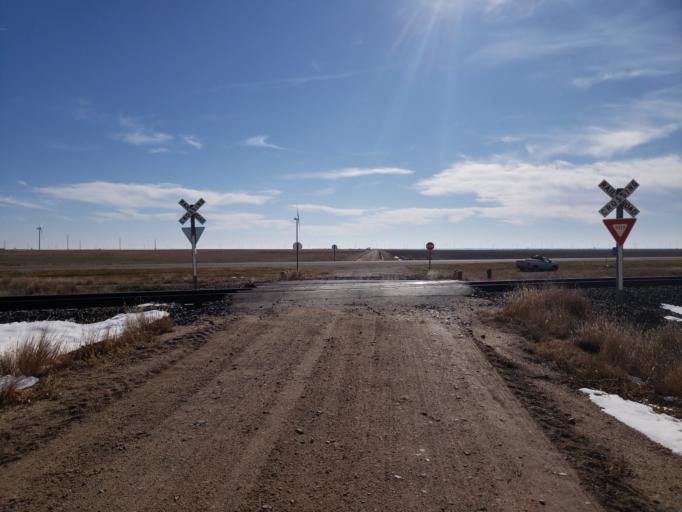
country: US
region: Kansas
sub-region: Ford County
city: Dodge City
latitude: 37.4781
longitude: -99.9248
